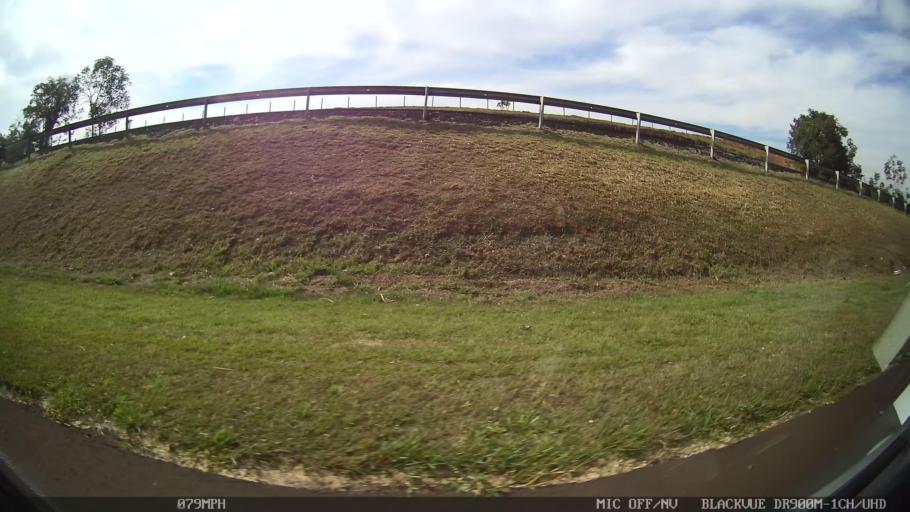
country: BR
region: Sao Paulo
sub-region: Matao
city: Matao
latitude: -21.6099
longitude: -48.4241
